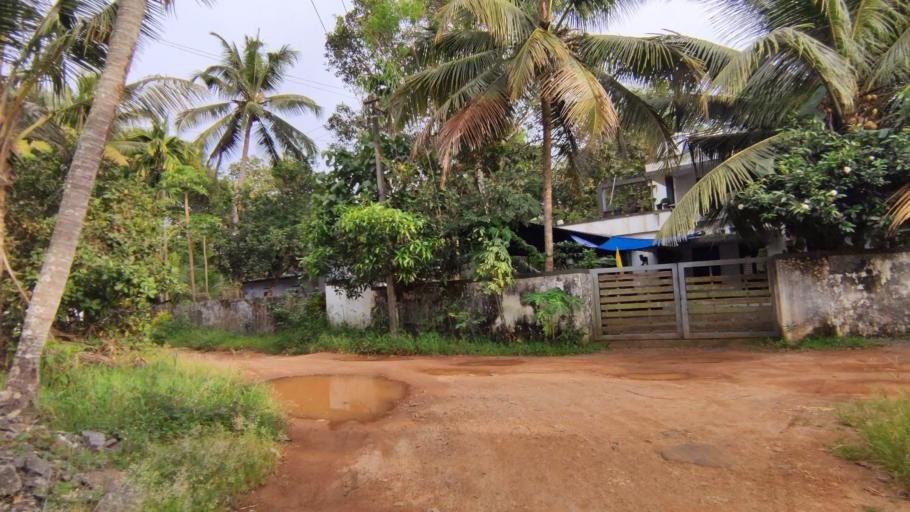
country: IN
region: Kerala
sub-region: Alappuzha
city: Shertallai
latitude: 9.6210
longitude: 76.3343
